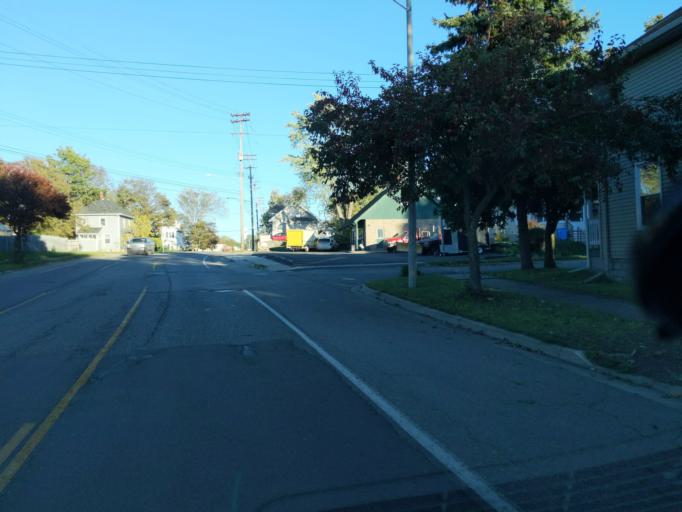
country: US
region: Michigan
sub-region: Ingham County
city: Lansing
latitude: 42.7298
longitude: -84.5300
